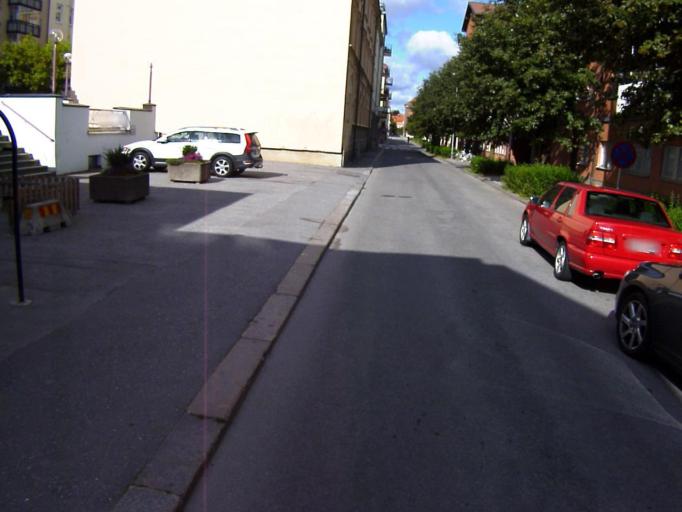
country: SE
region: Soedermanland
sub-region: Eskilstuna Kommun
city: Eskilstuna
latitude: 59.3694
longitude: 16.5097
